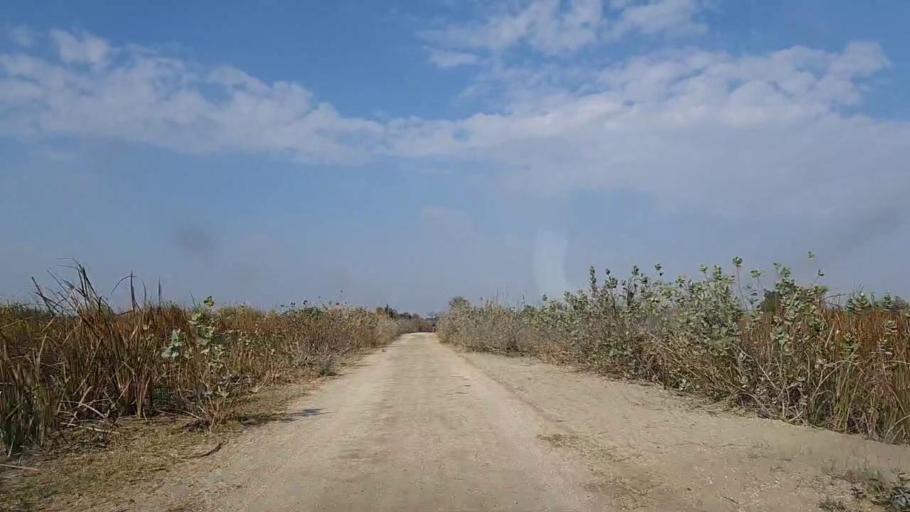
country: PK
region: Sindh
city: Sanghar
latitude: 26.2666
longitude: 69.0118
